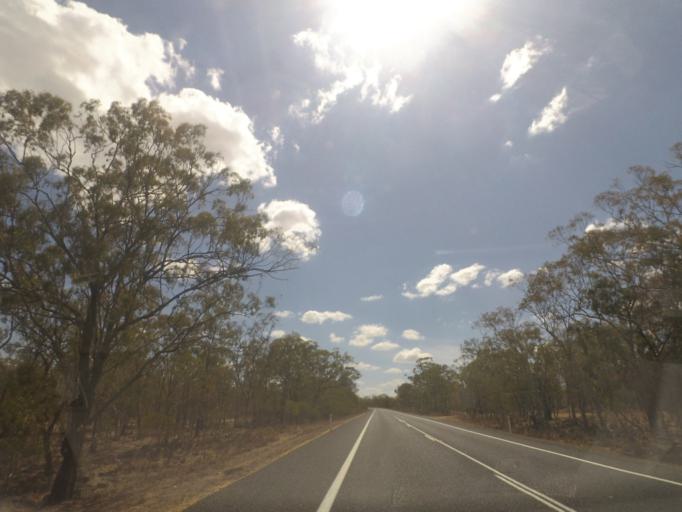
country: AU
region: Queensland
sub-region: Southern Downs
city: Warwick
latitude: -28.1629
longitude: 151.6796
